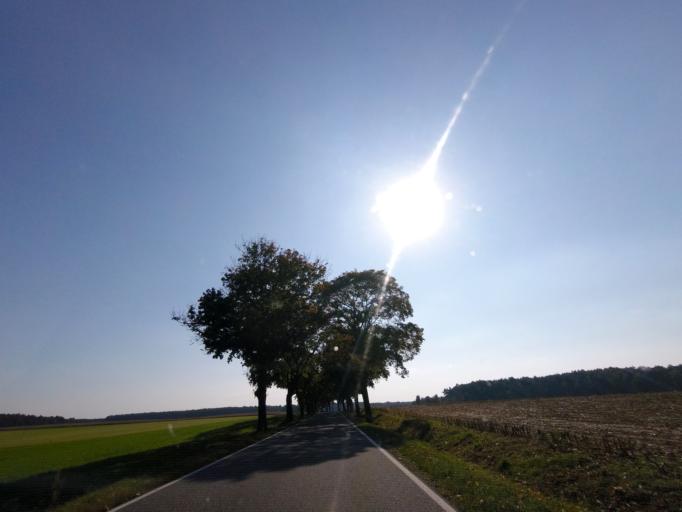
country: DE
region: Brandenburg
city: Niedergorsdorf
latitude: 51.9199
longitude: 13.0294
